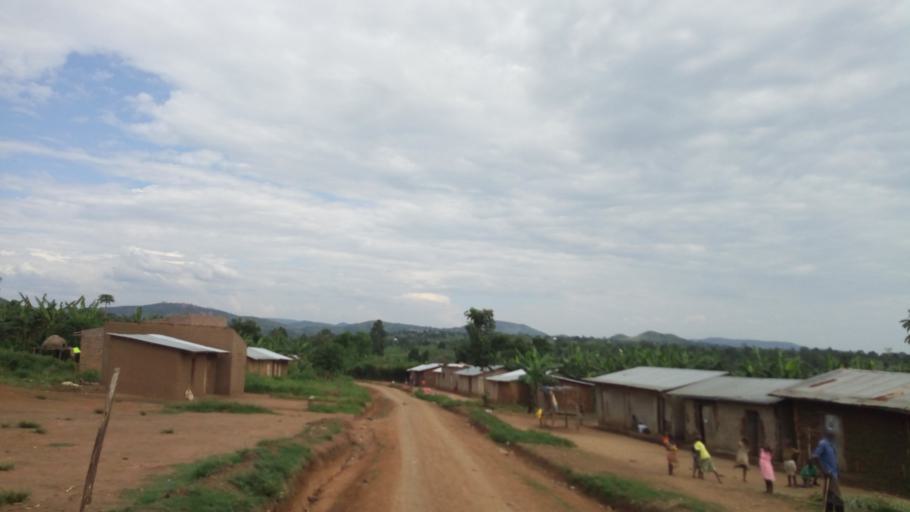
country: UG
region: Central Region
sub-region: Kiboga District
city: Kiboga
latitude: 0.7619
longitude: 31.6902
